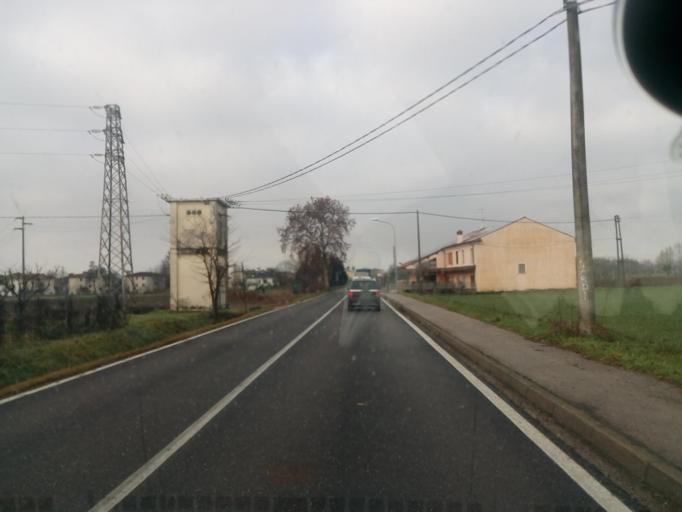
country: IT
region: Veneto
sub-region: Provincia di Vicenza
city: Bressanvido
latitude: 45.6635
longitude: 11.6422
